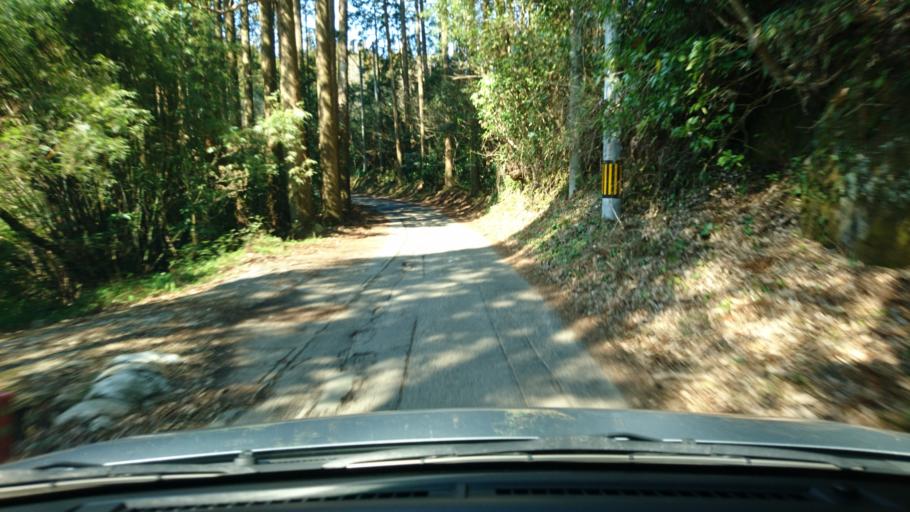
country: JP
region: Miyazaki
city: Miyazaki-shi
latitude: 31.8277
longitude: 131.3958
